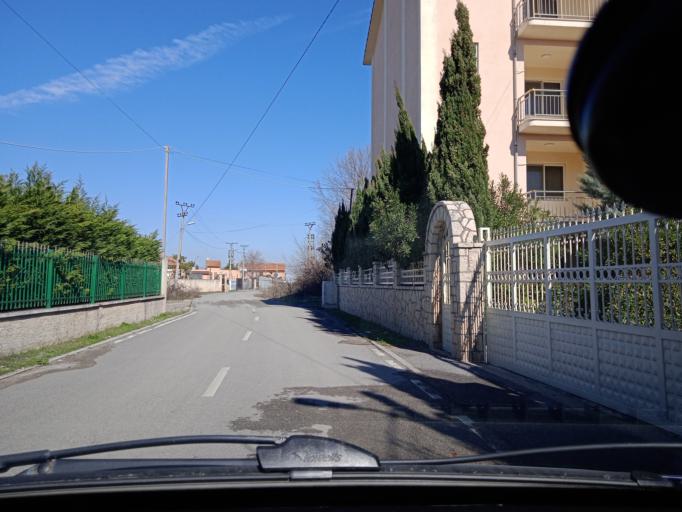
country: AL
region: Shkoder
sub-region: Rrethi i Shkodres
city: Velipoje
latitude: 41.8656
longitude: 19.4126
